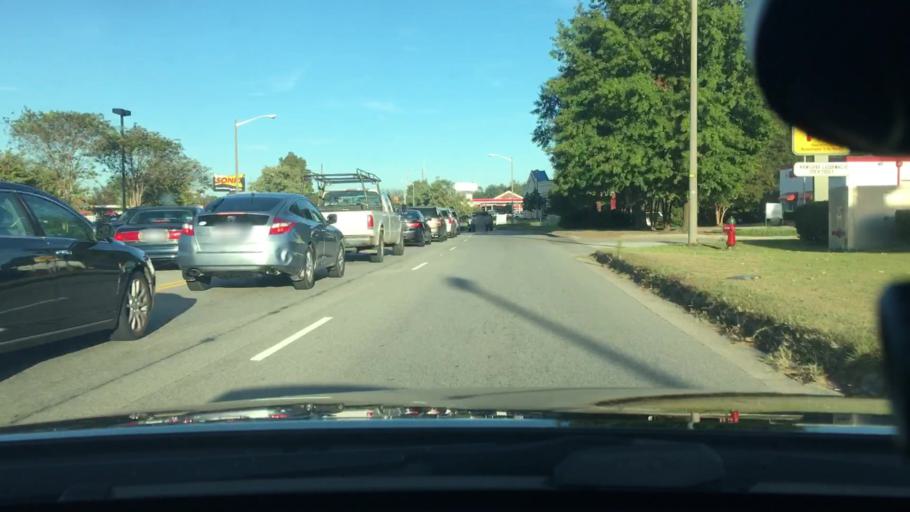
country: US
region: North Carolina
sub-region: Pitt County
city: Windsor
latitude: 35.5662
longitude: -77.3531
